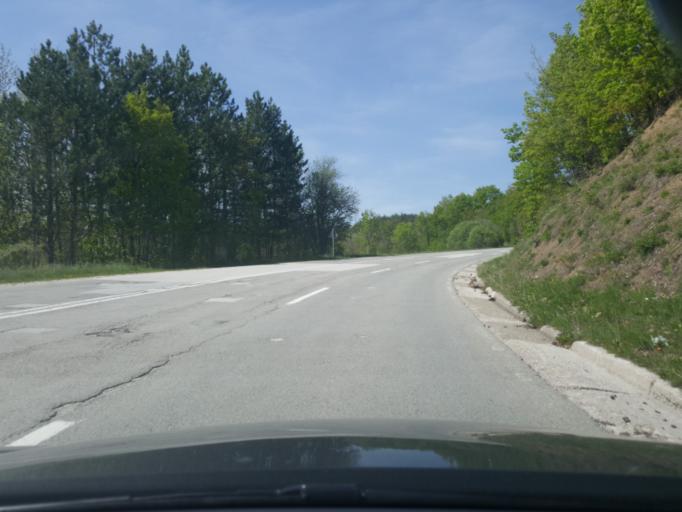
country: RS
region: Central Serbia
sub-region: Zlatiborski Okrug
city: Cajetina
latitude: 43.8106
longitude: 19.6449
